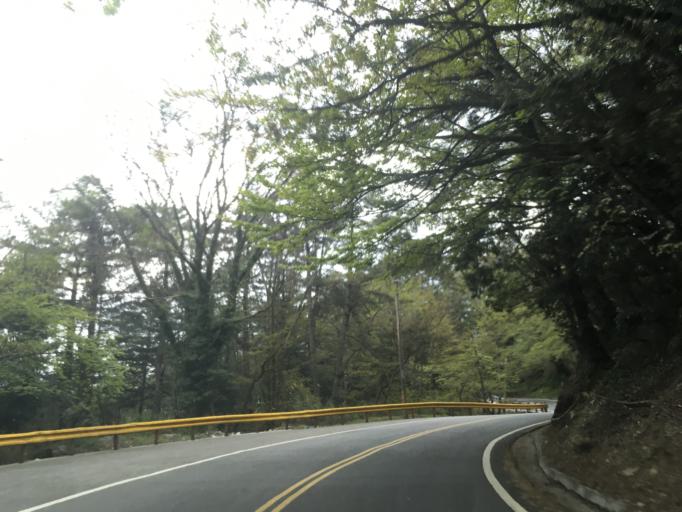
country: TW
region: Taiwan
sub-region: Hualien
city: Hualian
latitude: 24.1818
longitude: 121.3233
